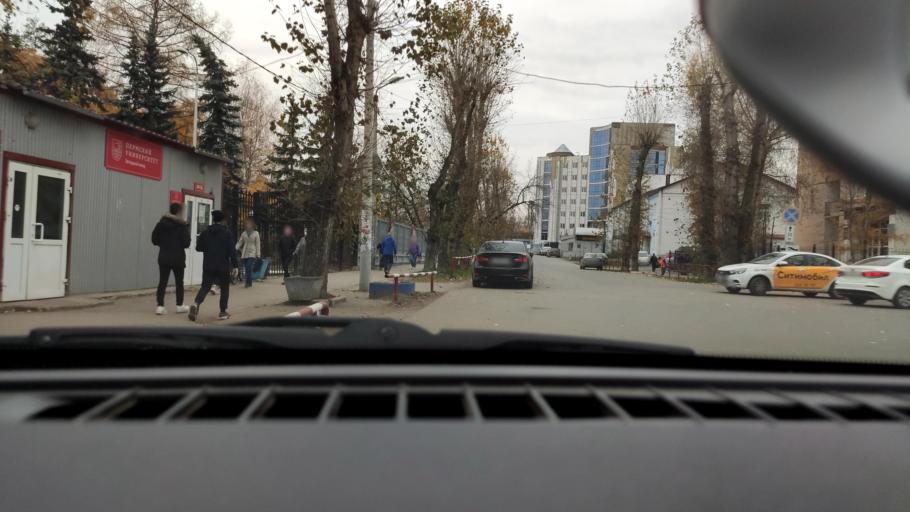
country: RU
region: Perm
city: Perm
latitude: 58.0073
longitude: 56.1837
